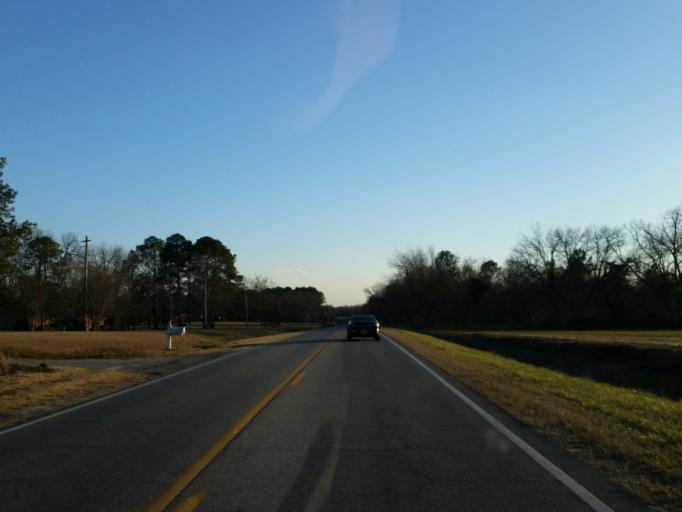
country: US
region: Georgia
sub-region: Crisp County
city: Cordele
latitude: 32.0111
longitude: -83.7927
